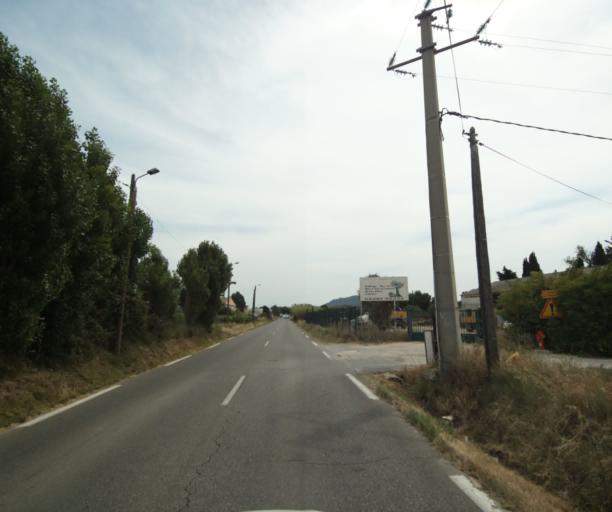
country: FR
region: Provence-Alpes-Cote d'Azur
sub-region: Departement du Var
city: La Farlede
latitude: 43.1403
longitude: 6.0425
